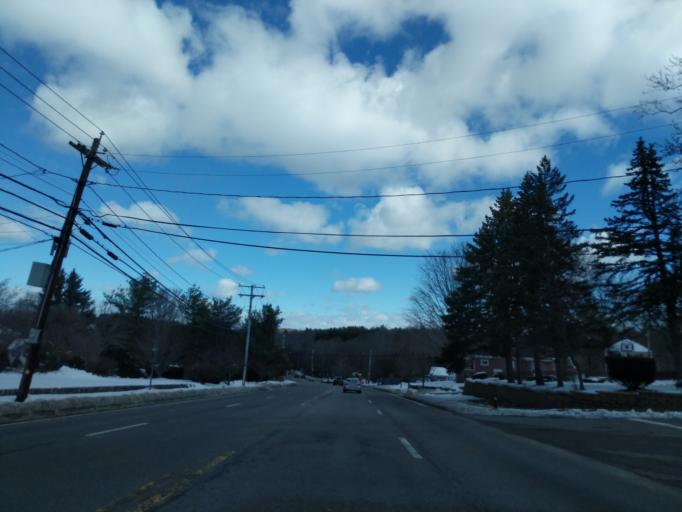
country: US
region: Massachusetts
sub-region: Norfolk County
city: Milton
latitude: 42.2335
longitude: -71.0702
